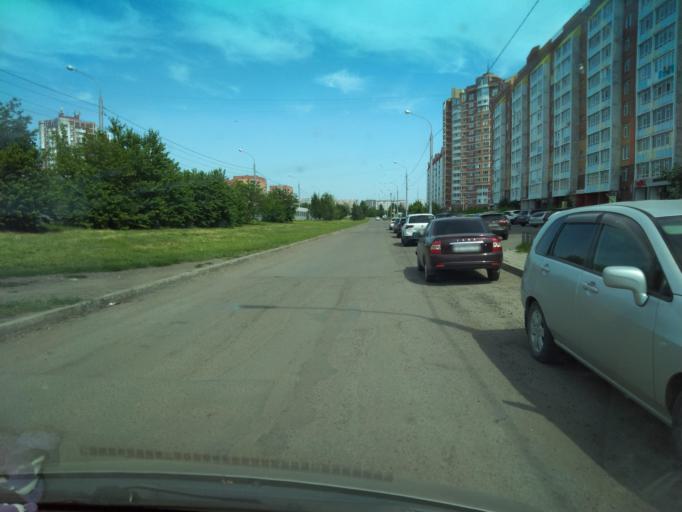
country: RU
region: Krasnoyarskiy
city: Krasnoyarsk
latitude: 56.0524
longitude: 92.9156
